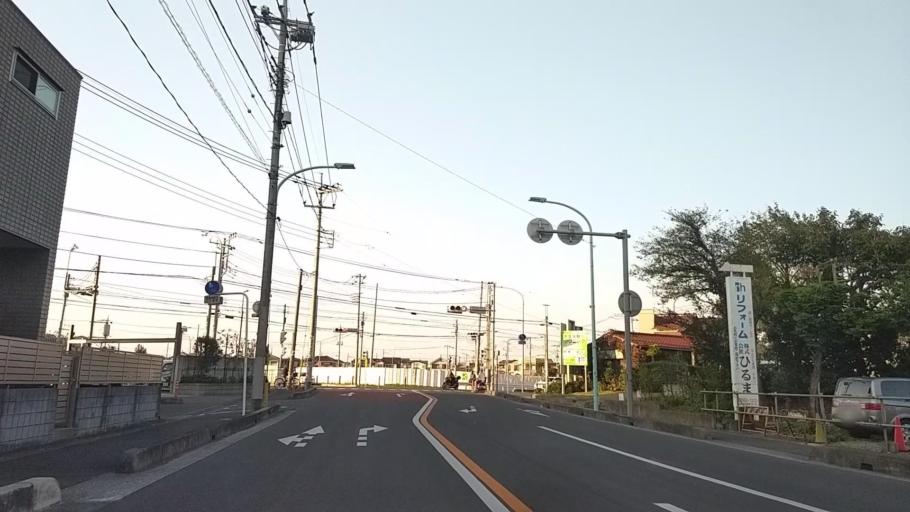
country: JP
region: Saitama
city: Tokorozawa
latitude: 35.8106
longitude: 139.4563
